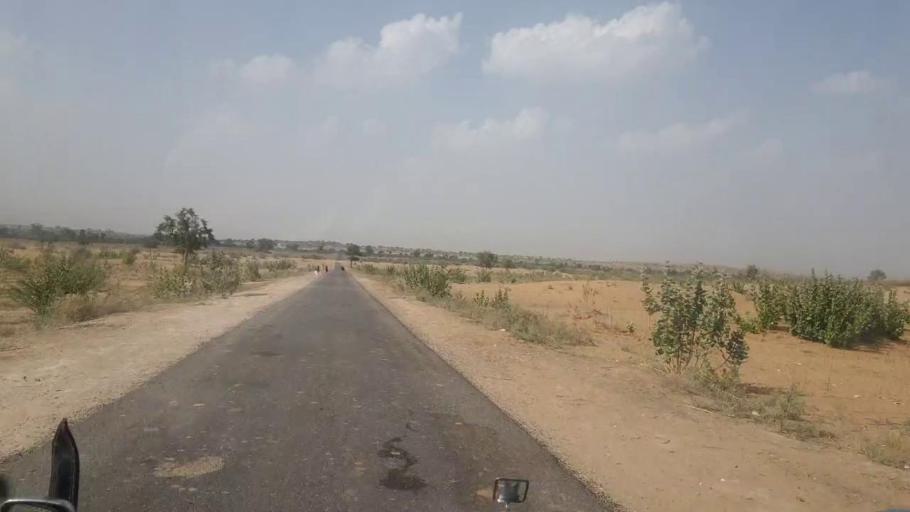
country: PK
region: Sindh
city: Islamkot
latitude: 25.2203
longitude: 70.2888
